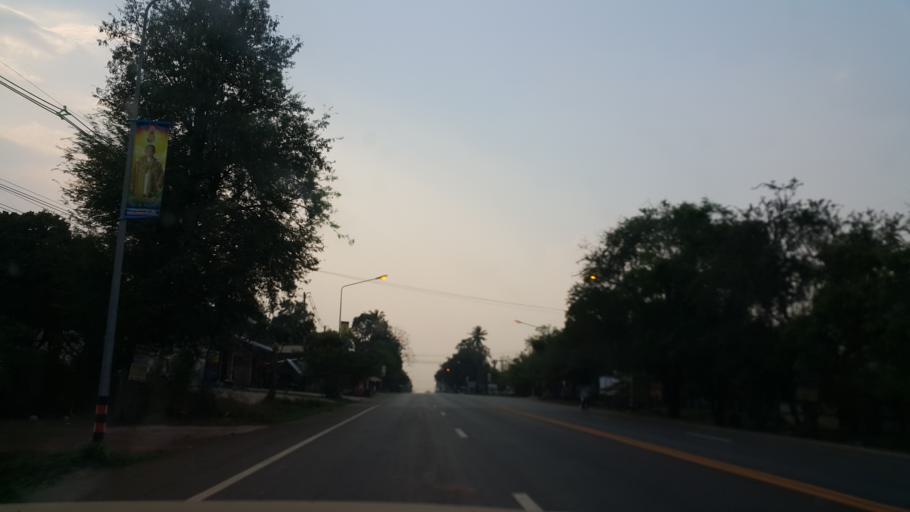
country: TH
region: Nakhon Phanom
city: Renu Nakhon
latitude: 17.0280
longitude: 104.7122
